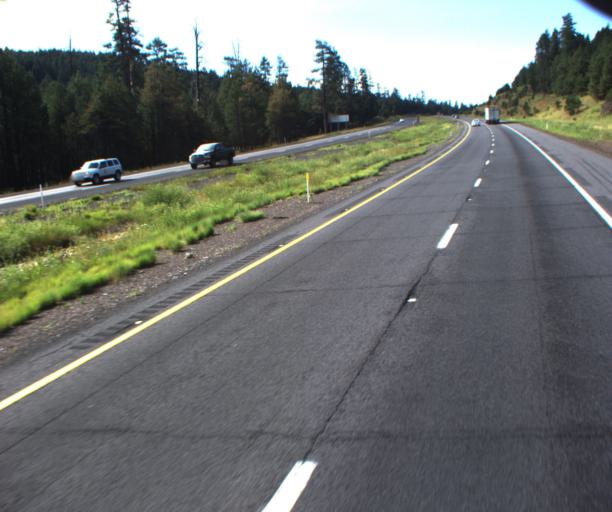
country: US
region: Arizona
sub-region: Coconino County
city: Mountainaire
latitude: 35.0407
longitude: -111.6854
